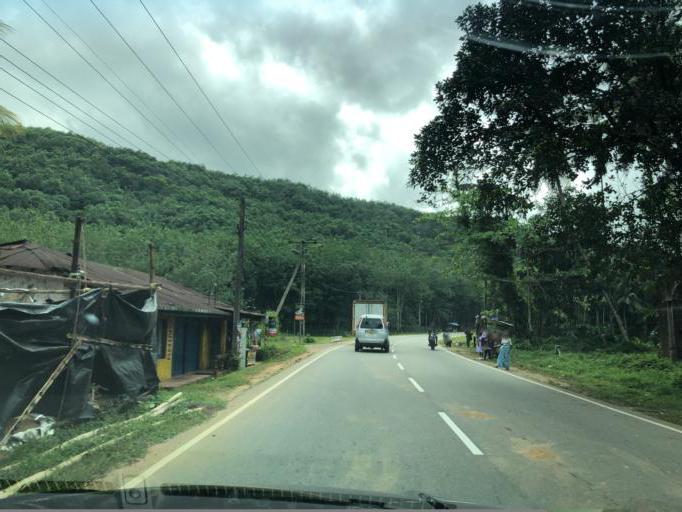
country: LK
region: Western
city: Horana South
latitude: 6.6803
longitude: 80.1488
